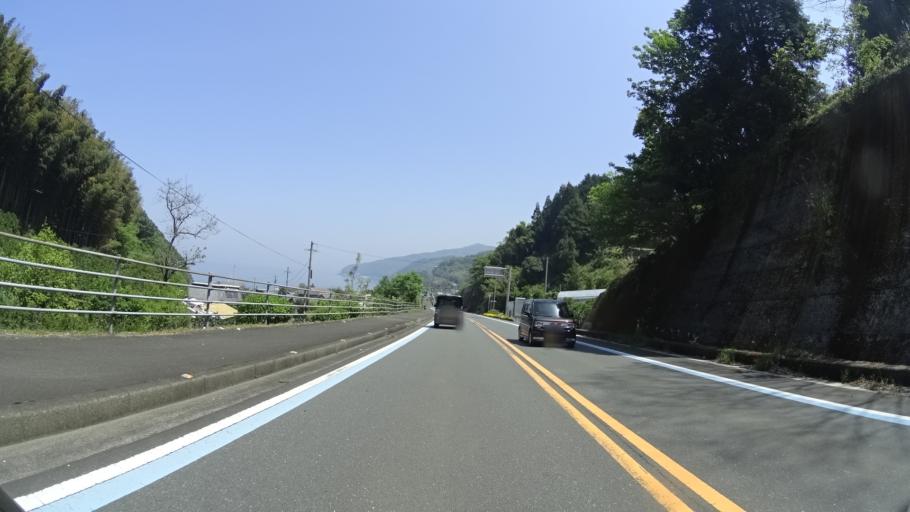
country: JP
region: Ehime
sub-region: Nishiuwa-gun
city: Ikata-cho
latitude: 33.5392
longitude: 132.4131
